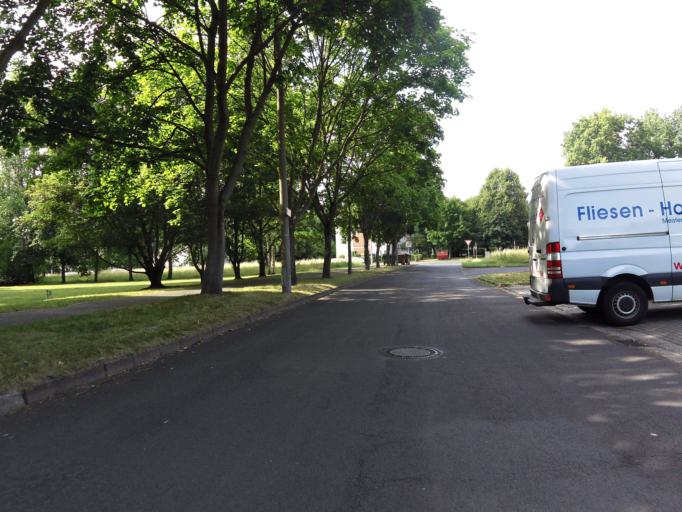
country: DE
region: Saxony
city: Leipzig
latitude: 51.3567
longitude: 12.4219
